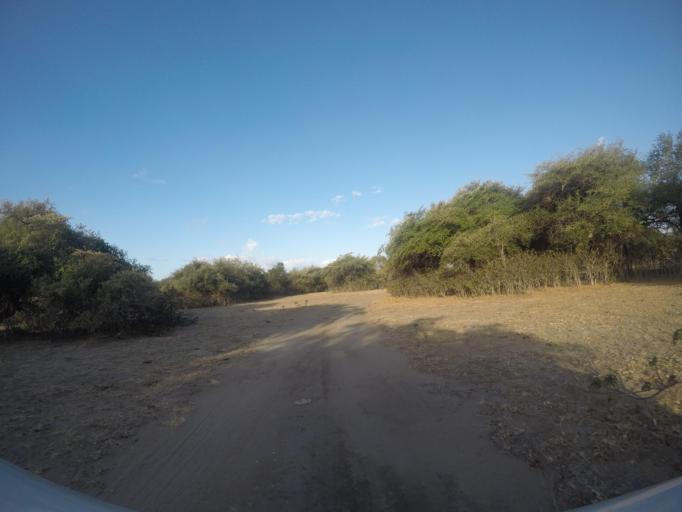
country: TL
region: Lautem
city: Lospalos
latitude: -8.3233
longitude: 126.9985
